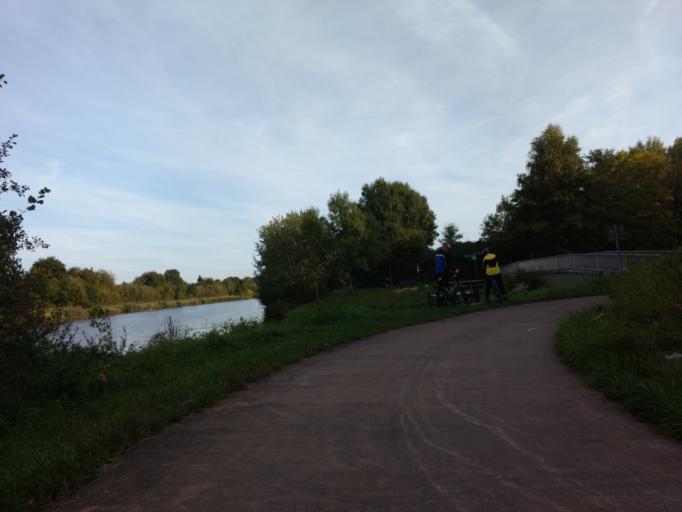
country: DE
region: Saarland
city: Saarlouis
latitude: 49.3279
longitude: 6.7375
